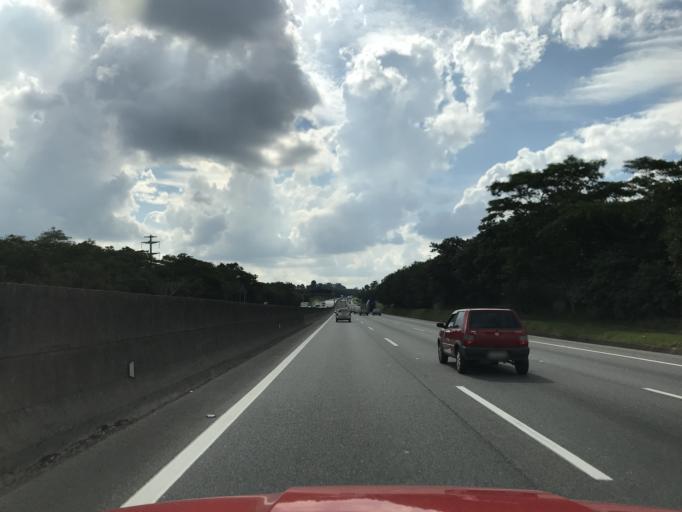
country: BR
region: Sao Paulo
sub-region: Jundiai
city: Jundiai
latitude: -23.1634
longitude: -46.9301
